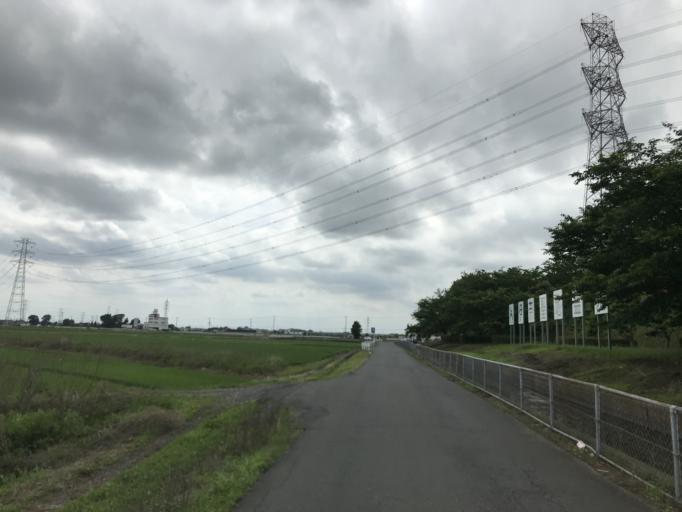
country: JP
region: Ibaraki
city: Moriya
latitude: 35.9786
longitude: 140.0438
